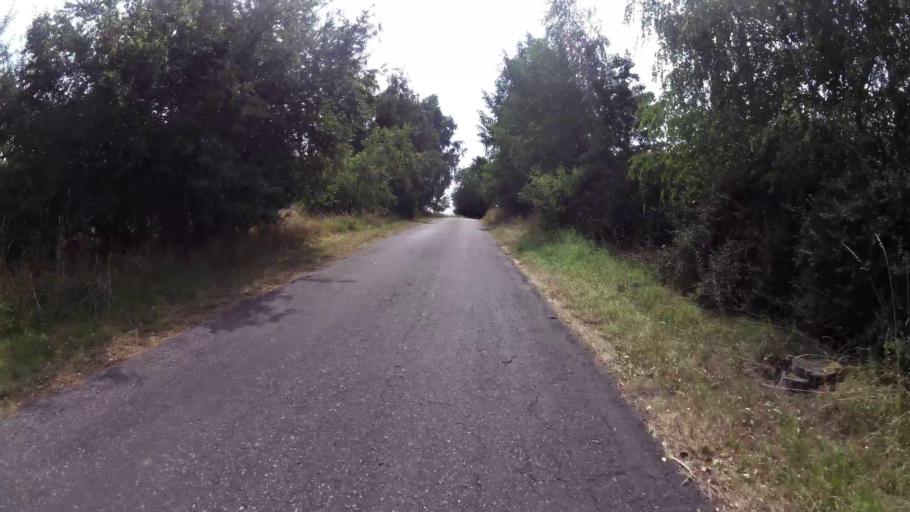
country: PL
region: West Pomeranian Voivodeship
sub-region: Powiat gryfinski
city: Mieszkowice
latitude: 52.8775
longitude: 14.5272
